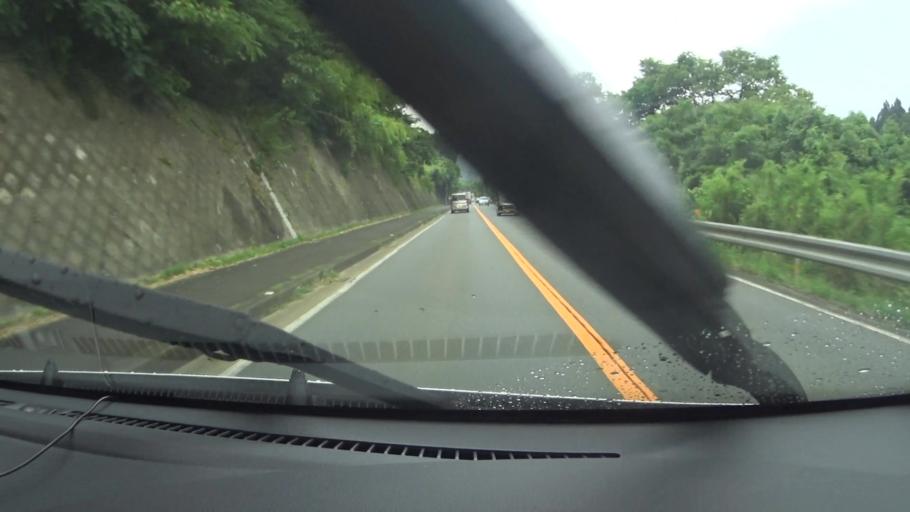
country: JP
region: Kyoto
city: Ayabe
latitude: 35.2542
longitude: 135.4155
